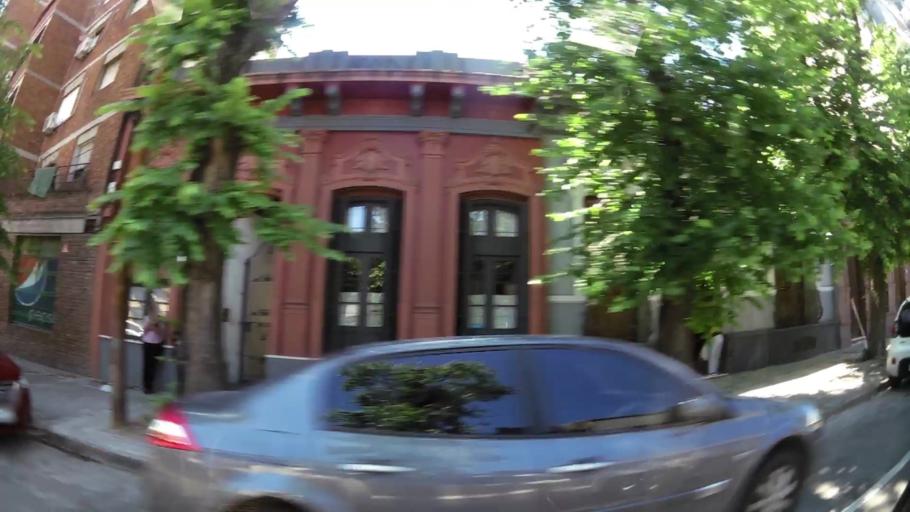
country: UY
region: Montevideo
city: Montevideo
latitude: -34.9065
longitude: -56.1745
